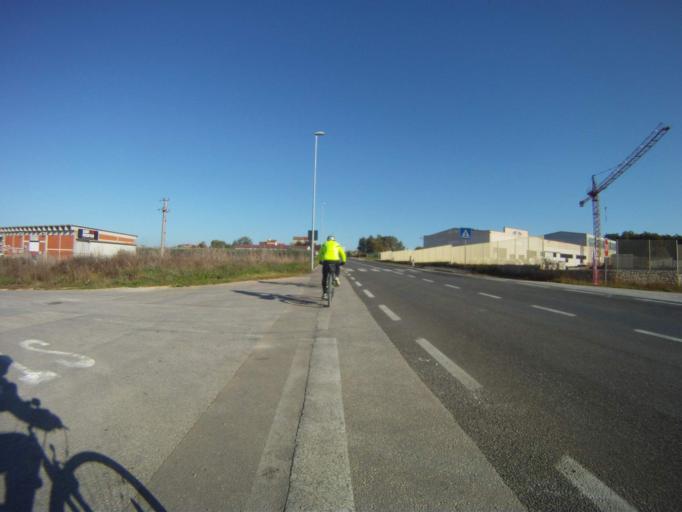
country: HR
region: Istarska
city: Novigrad
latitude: 45.3296
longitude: 13.5766
